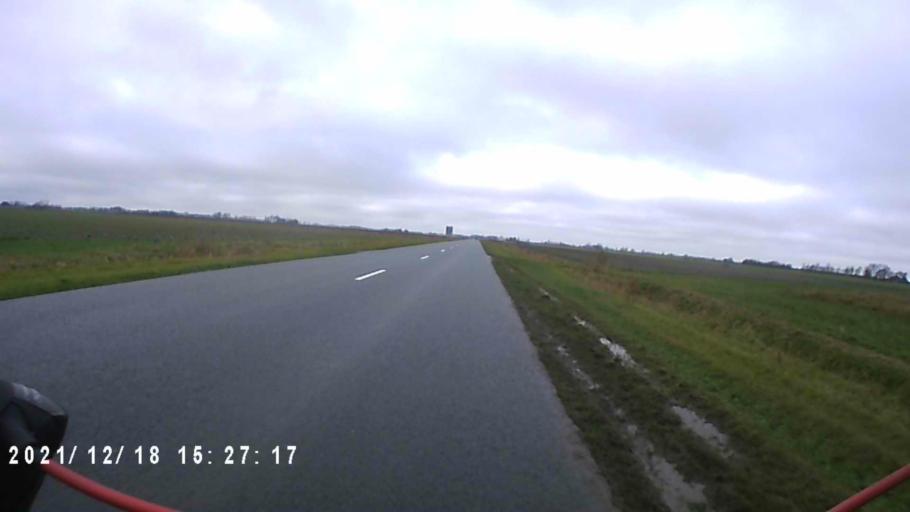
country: NL
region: Friesland
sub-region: Gemeente Dongeradeel
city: Anjum
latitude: 53.3291
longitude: 6.1475
